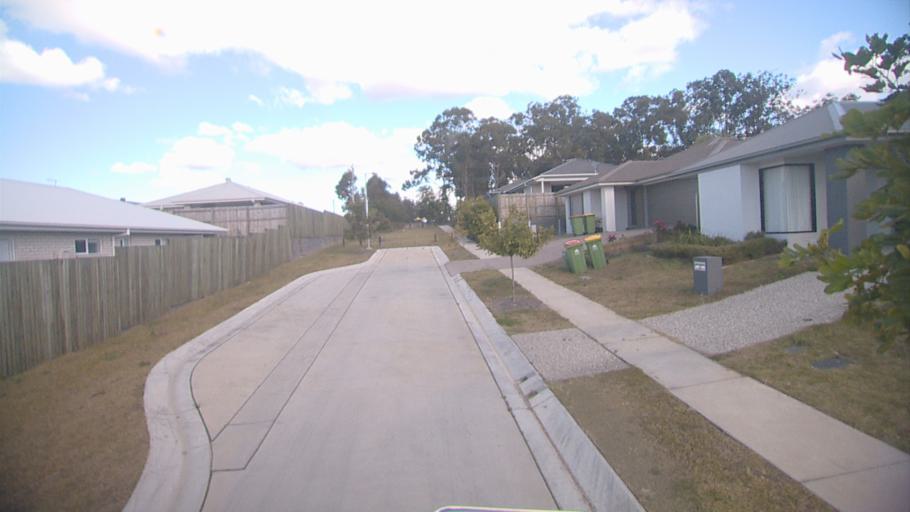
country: AU
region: Queensland
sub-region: Logan
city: Logan Reserve
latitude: -27.7165
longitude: 153.0851
